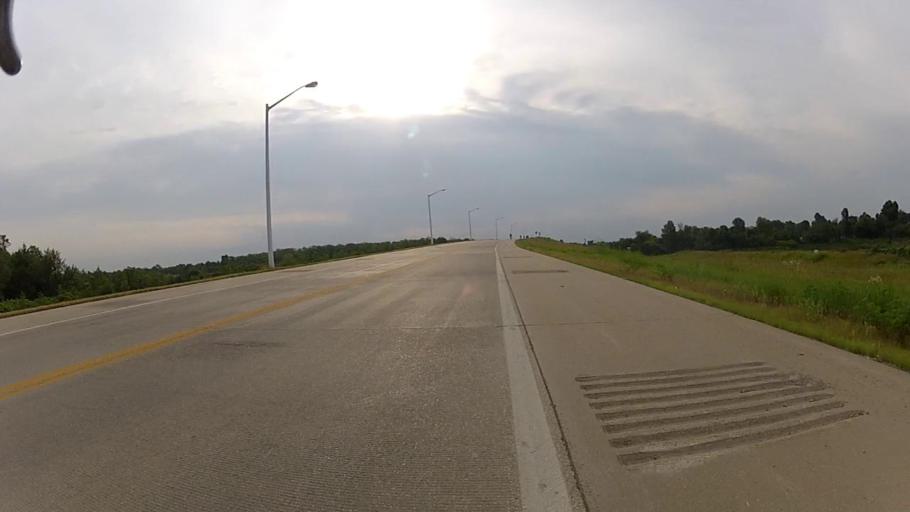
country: US
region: Kansas
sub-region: Cherokee County
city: Columbus
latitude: 37.1789
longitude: -94.8390
